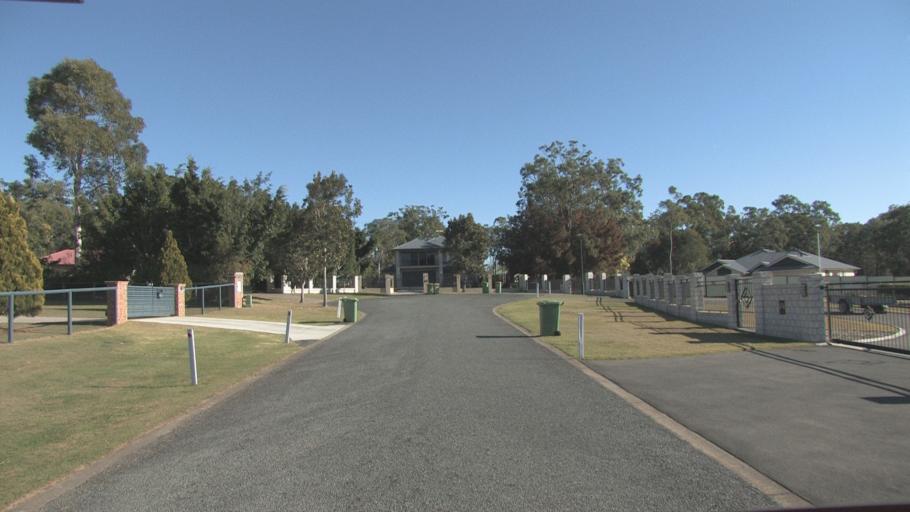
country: AU
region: Queensland
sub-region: Logan
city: North Maclean
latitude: -27.7407
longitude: 152.9620
